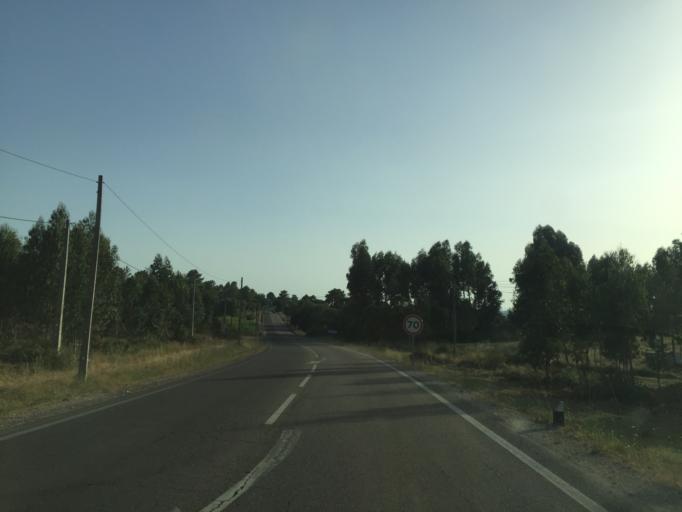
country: PT
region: Santarem
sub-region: Entroncamento
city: Entroncamento
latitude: 39.4873
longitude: -8.4449
